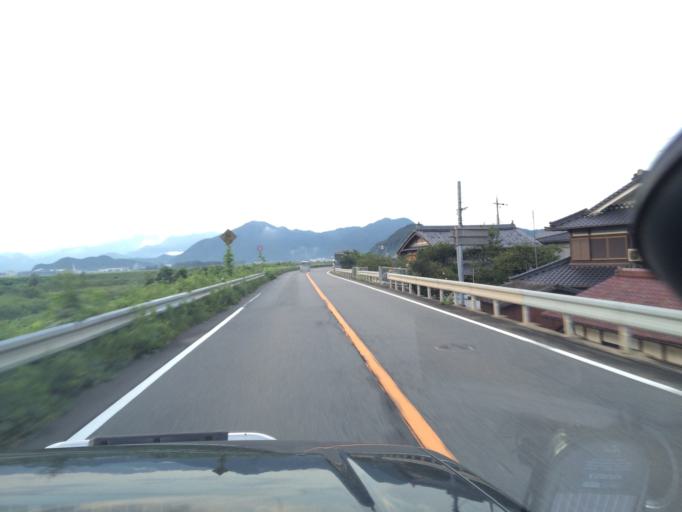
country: JP
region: Hyogo
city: Nishiwaki
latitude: 35.1424
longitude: 135.0291
